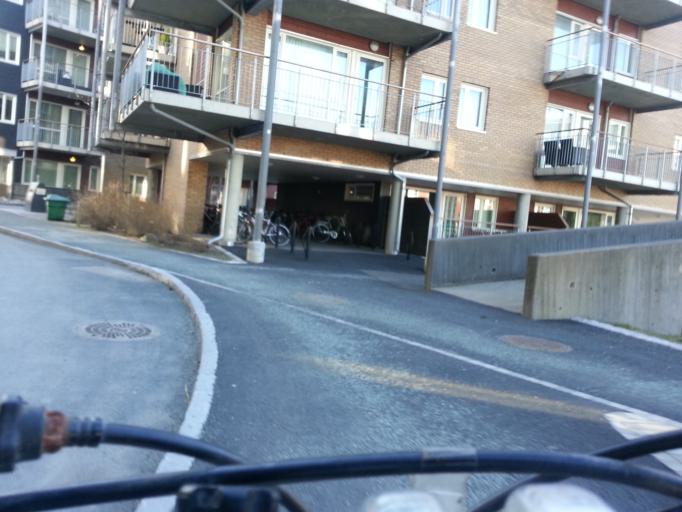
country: NO
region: Sor-Trondelag
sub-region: Trondheim
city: Trondheim
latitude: 63.4367
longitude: 10.4103
